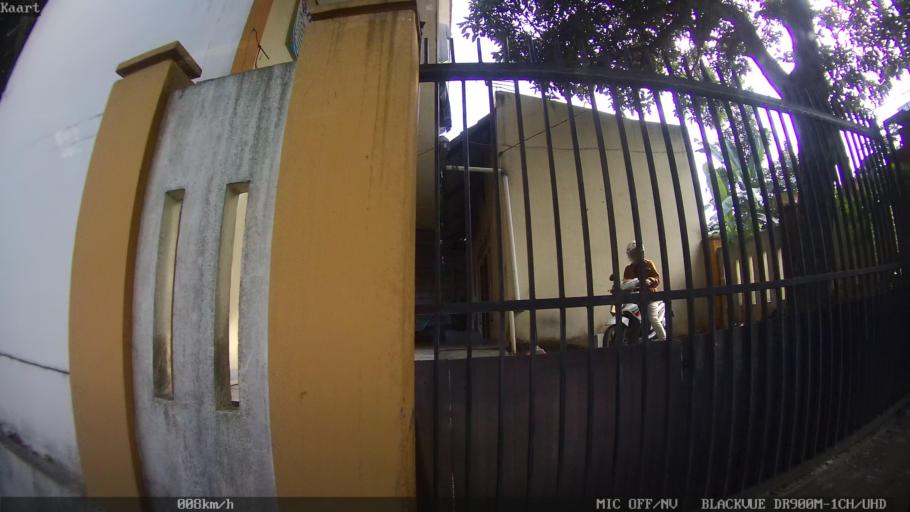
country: ID
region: Lampung
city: Kedaton
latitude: -5.3902
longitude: 105.2216
